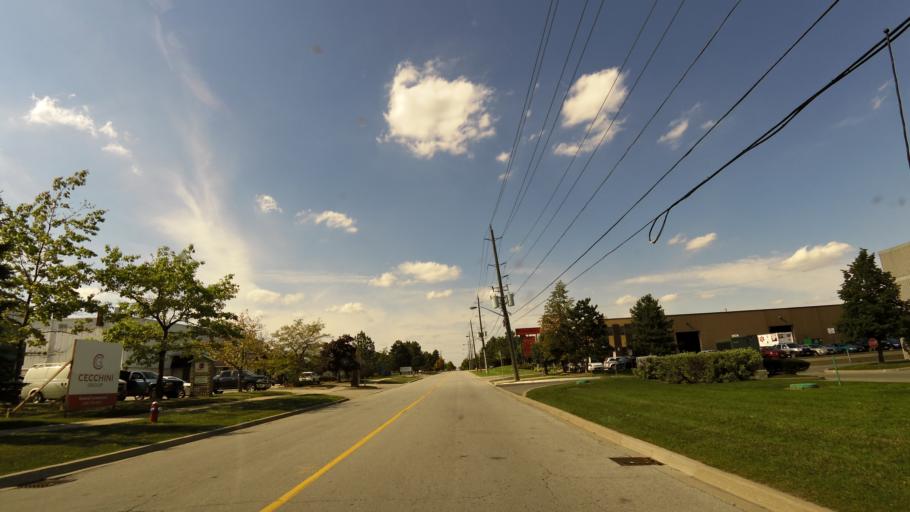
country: CA
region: Ontario
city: Brampton
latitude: 43.7216
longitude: -79.6821
